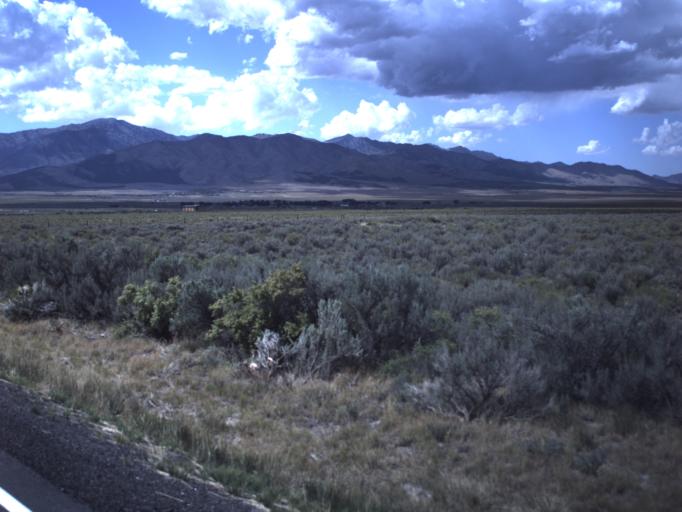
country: US
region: Utah
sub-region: Tooele County
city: Tooele
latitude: 40.3370
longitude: -112.4168
